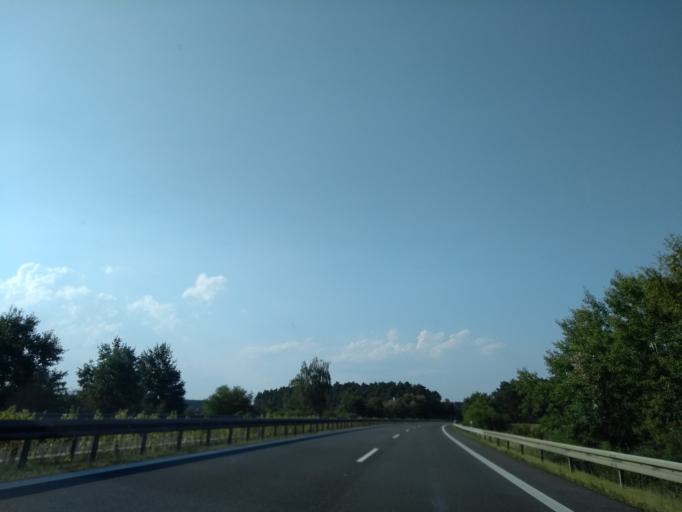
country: DE
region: Brandenburg
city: Calau
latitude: 51.7426
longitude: 13.8621
